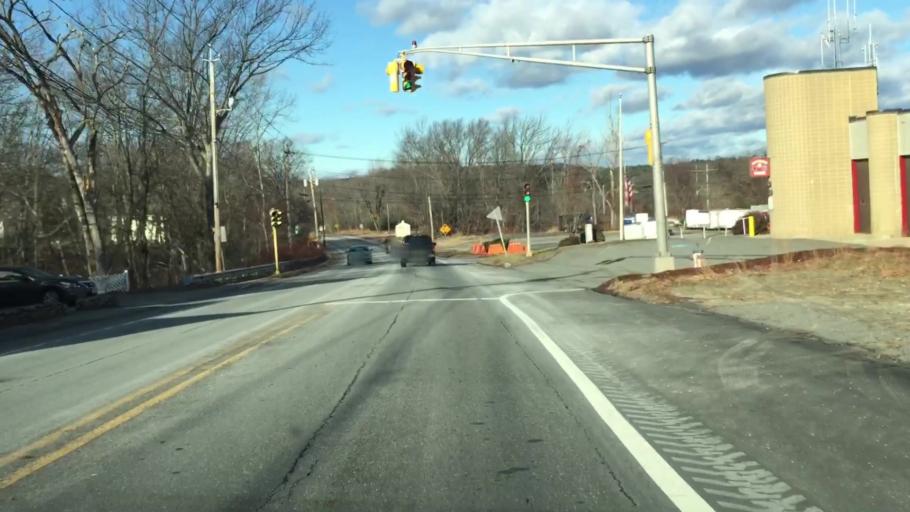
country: US
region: Massachusetts
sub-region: Worcester County
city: West Boylston
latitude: 42.3667
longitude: -71.7816
